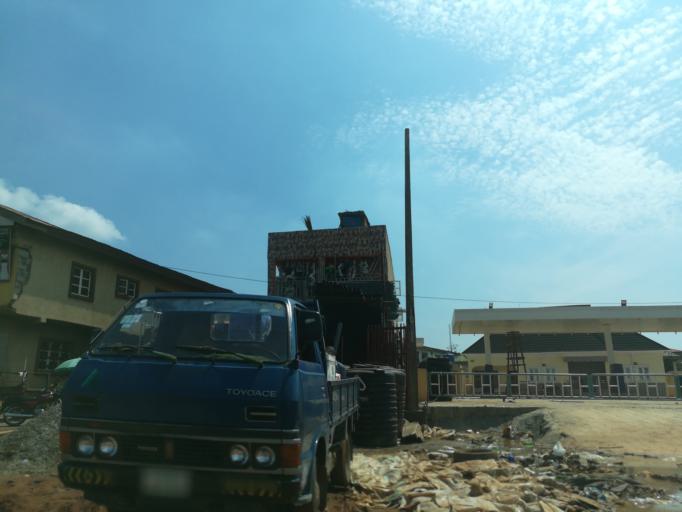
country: NG
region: Lagos
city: Ikorodu
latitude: 6.6469
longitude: 3.4788
